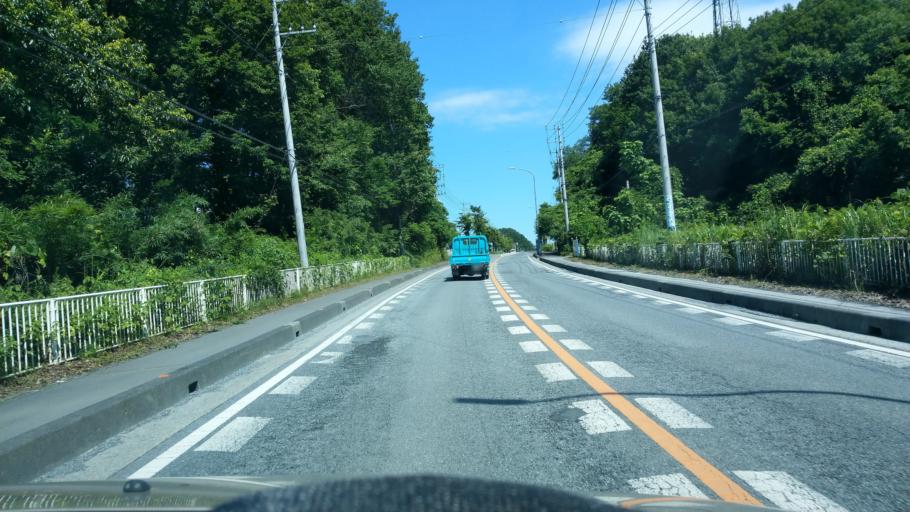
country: JP
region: Saitama
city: Ogawa
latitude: 36.0734
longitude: 139.2467
